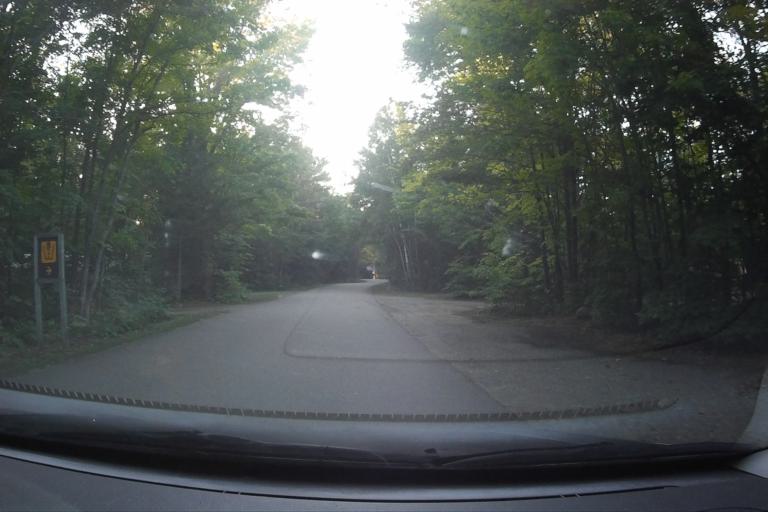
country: CA
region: Ontario
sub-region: Algoma
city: Sault Ste. Marie
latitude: 46.9692
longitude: -84.6847
